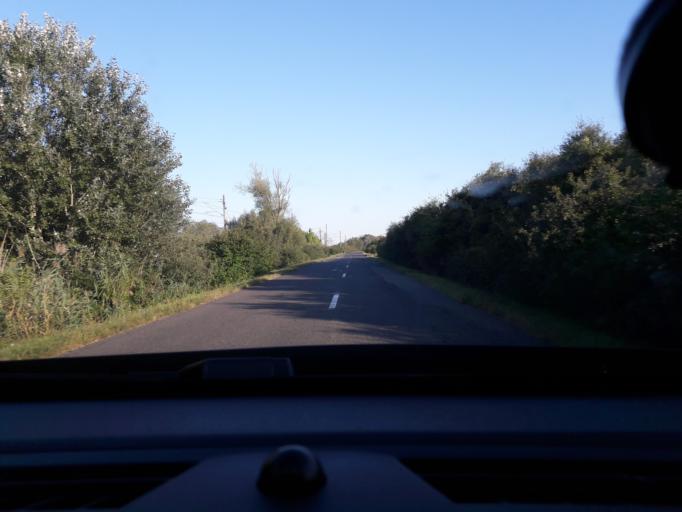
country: SK
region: Kosicky
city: Michalovce
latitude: 48.6179
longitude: 21.9421
